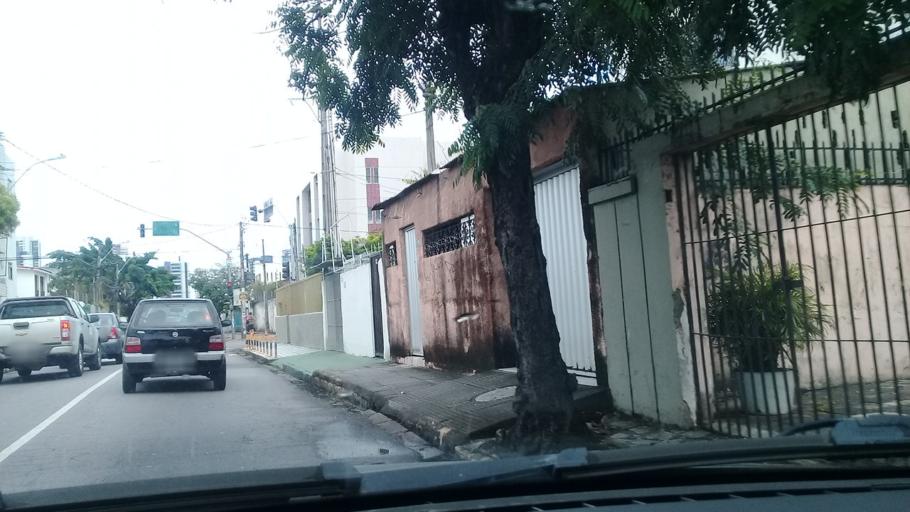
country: BR
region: Pernambuco
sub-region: Recife
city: Recife
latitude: -8.1351
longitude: -34.9123
